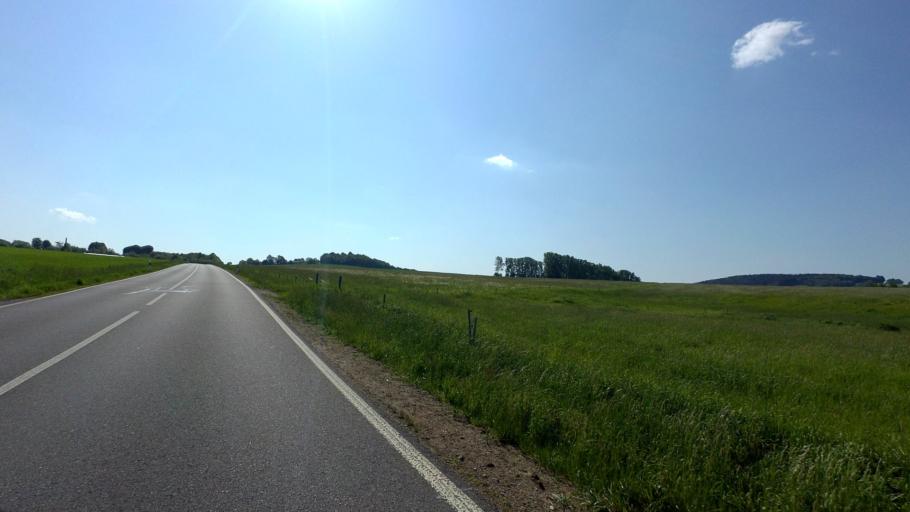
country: DE
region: Saxony
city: Neustadt in Sachsen
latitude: 51.0337
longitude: 14.1740
